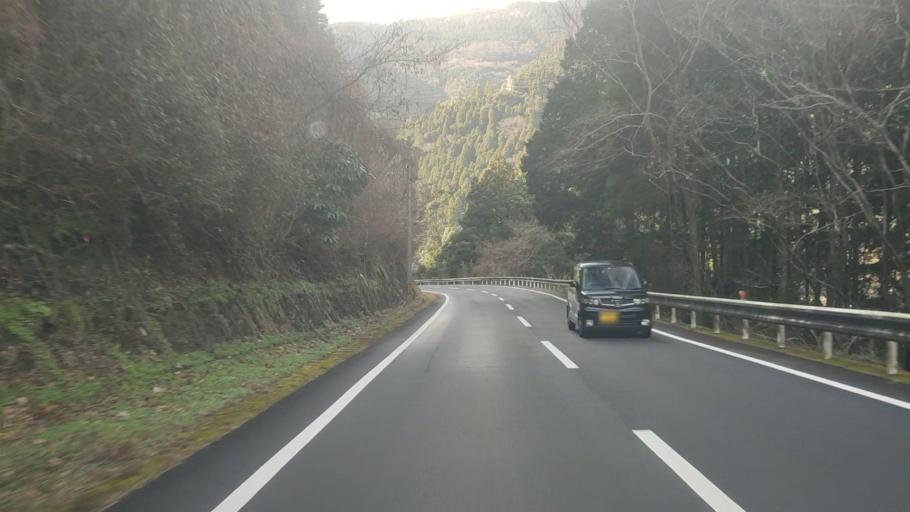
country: JP
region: Kumamoto
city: Hitoyoshi
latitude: 32.3234
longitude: 130.8407
